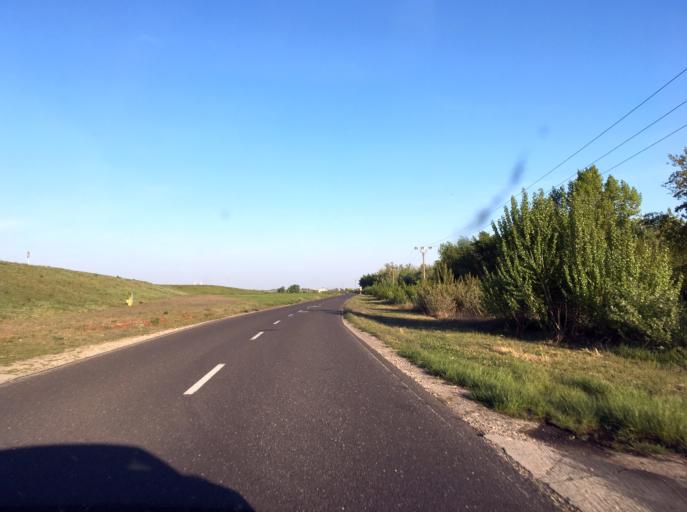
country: SK
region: Trnavsky
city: Samorin
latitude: 47.9960
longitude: 17.3333
